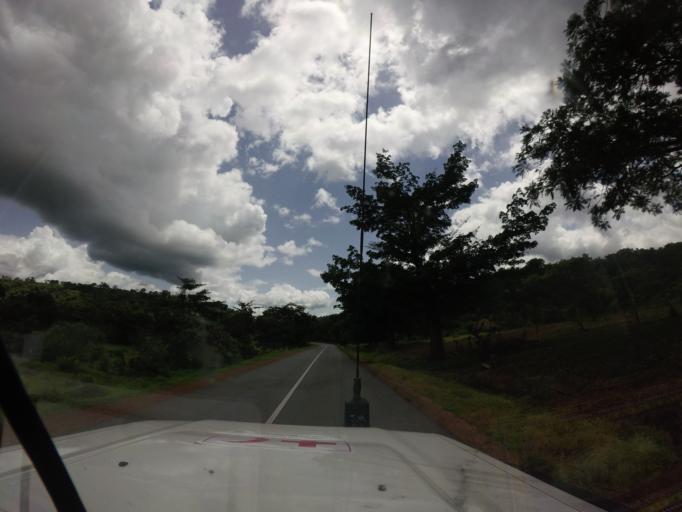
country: SL
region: Northern Province
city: Bindi
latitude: 10.1495
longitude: -11.5580
